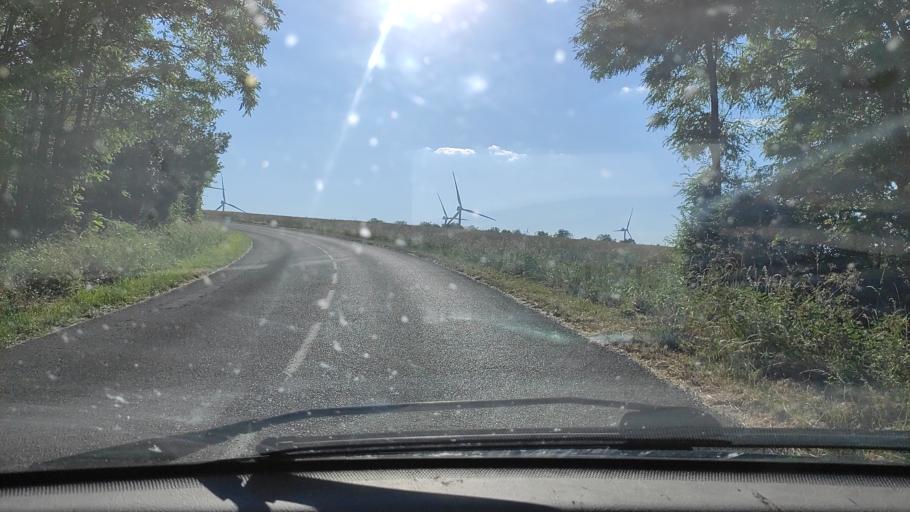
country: FR
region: Poitou-Charentes
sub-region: Departement des Deux-Sevres
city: Saint-Varent
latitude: 46.8599
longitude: -0.2045
